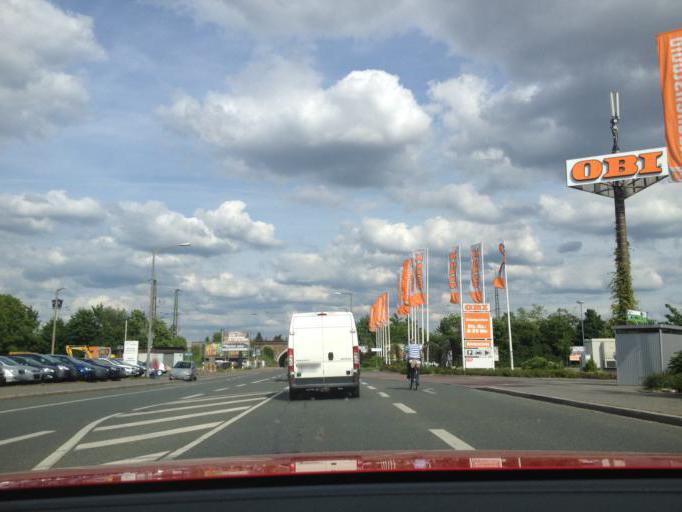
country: DE
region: Bavaria
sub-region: Regierungsbezirk Mittelfranken
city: Grossreuth bei Schweinau
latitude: 49.4535
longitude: 11.0179
